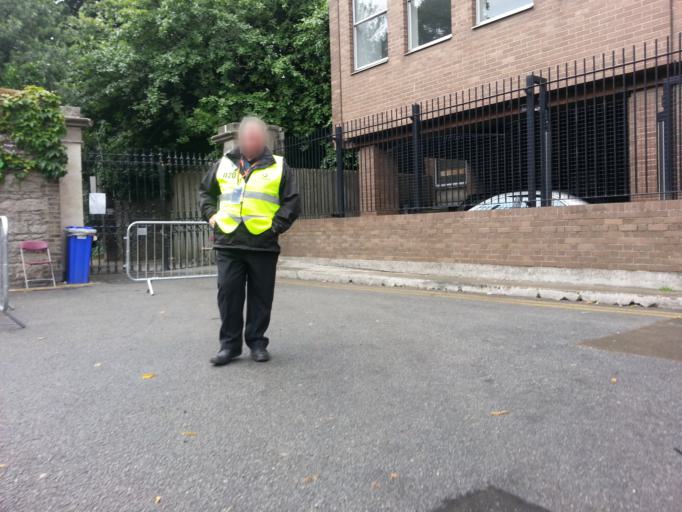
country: IE
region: Leinster
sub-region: Dublin City
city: Dublin
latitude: 53.3360
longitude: -6.2623
